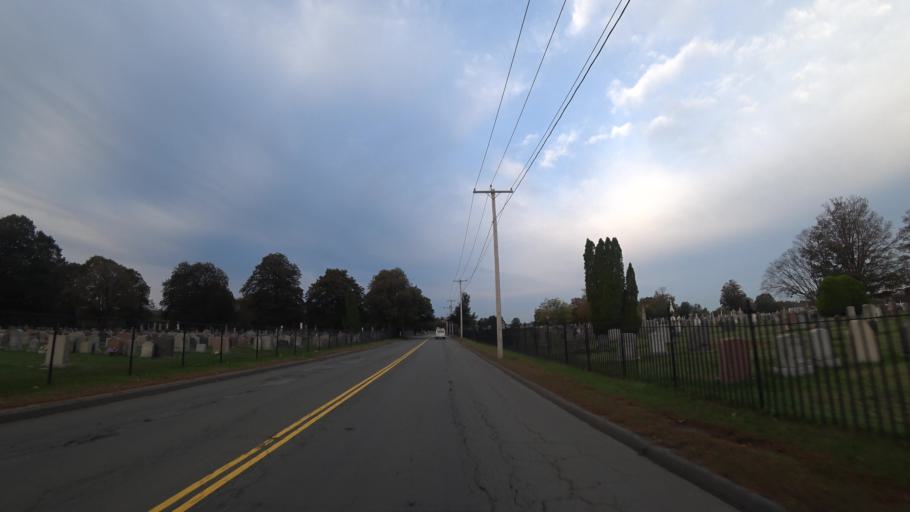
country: US
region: Massachusetts
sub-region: Middlesex County
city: Everett
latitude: 42.4282
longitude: -71.0341
